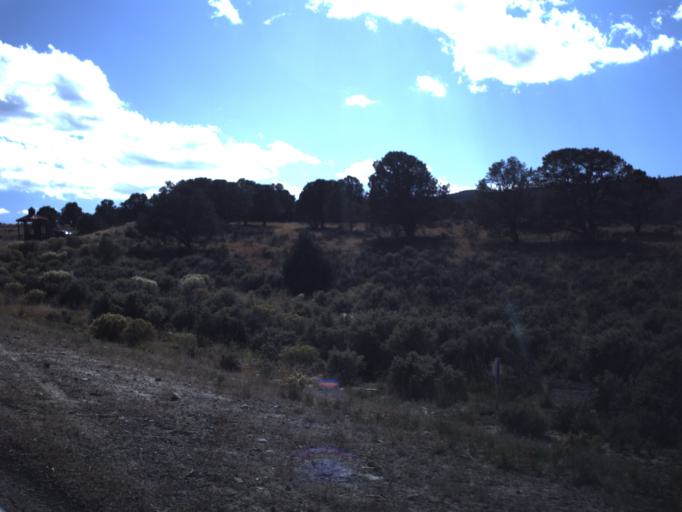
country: US
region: Utah
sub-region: Garfield County
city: Panguitch
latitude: 37.8033
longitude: -112.4353
